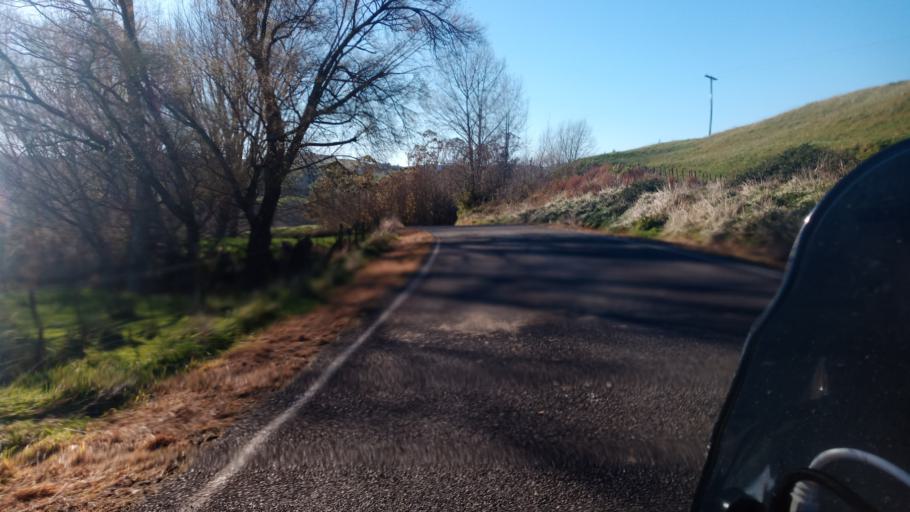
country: NZ
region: Hawke's Bay
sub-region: Wairoa District
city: Wairoa
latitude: -38.8221
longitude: 177.2905
